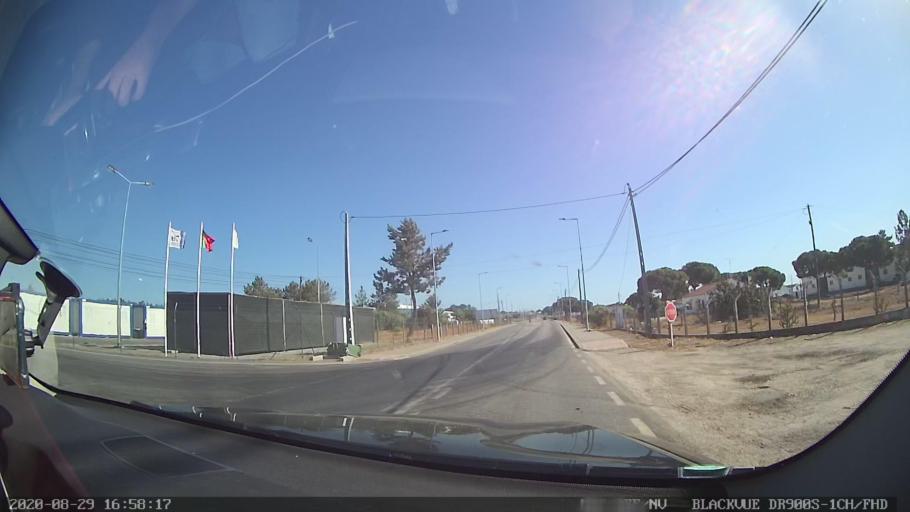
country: PT
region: Setubal
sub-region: Alcacer do Sal
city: Alcacer do Sal
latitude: 38.3972
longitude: -8.5144
